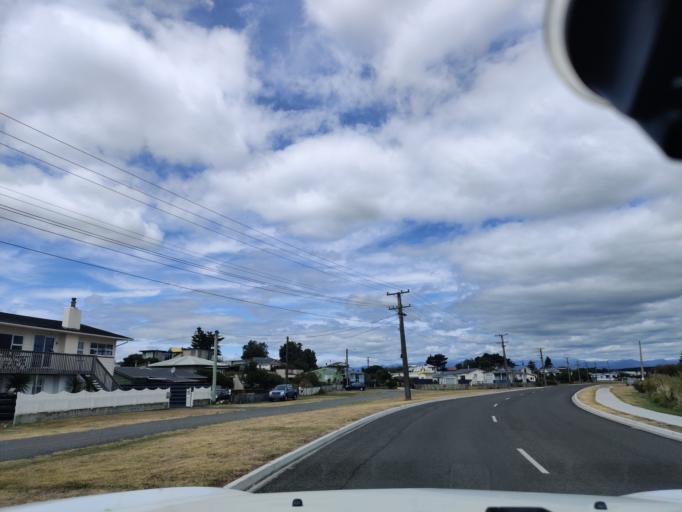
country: NZ
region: Manawatu-Wanganui
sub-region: Horowhenua District
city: Foxton
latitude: -40.4616
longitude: 175.2247
